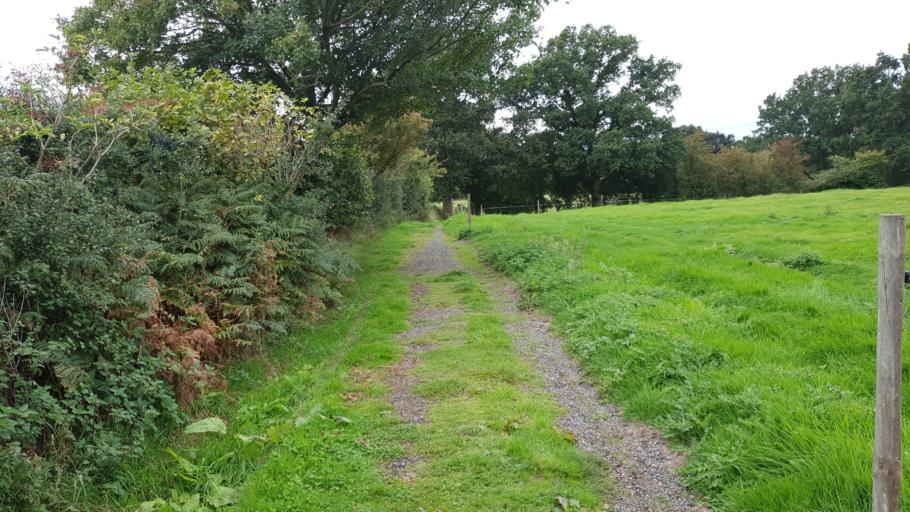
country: GB
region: England
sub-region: Suffolk
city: East Bergholt
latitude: 51.9468
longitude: 1.0035
